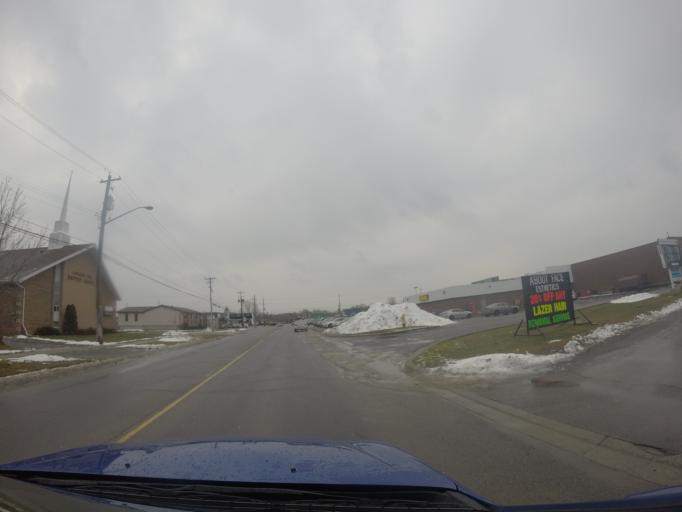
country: CA
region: Ontario
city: Greater Sudbury
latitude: 46.5234
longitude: -80.9293
